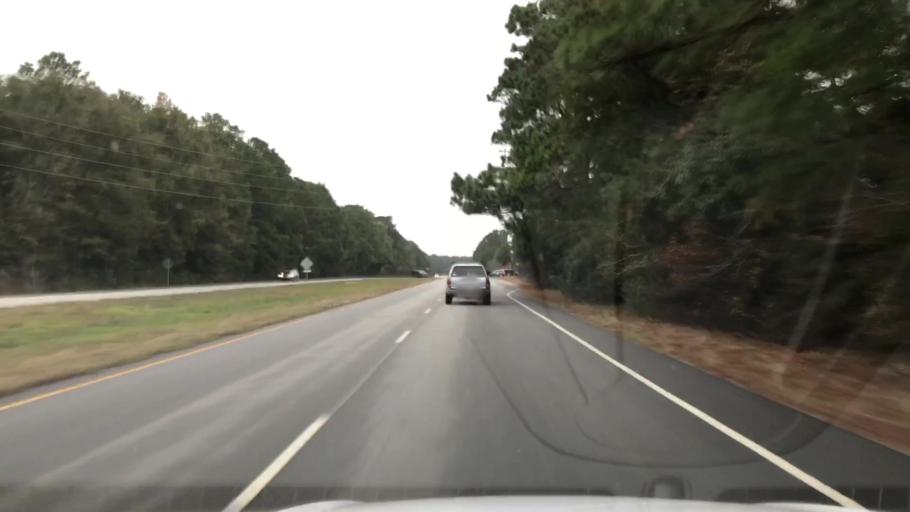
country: US
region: South Carolina
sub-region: Charleston County
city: Awendaw
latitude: 32.9275
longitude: -79.7140
